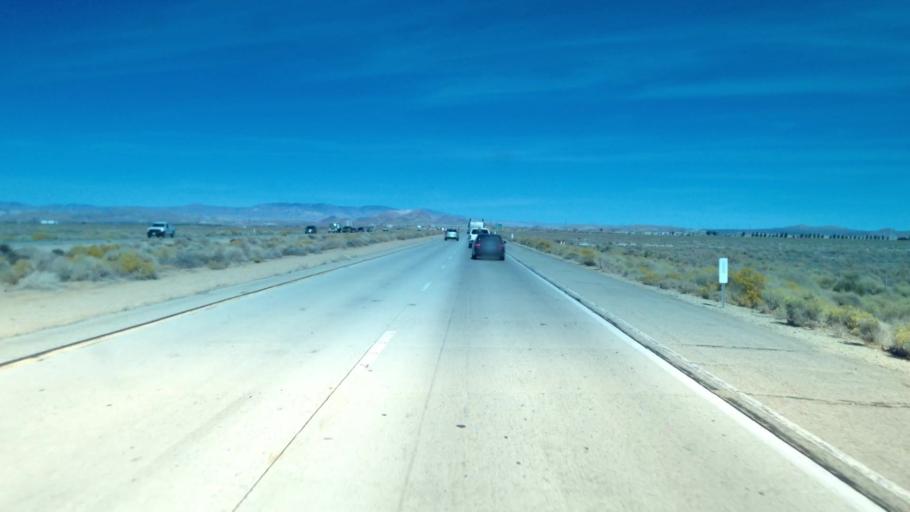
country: US
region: California
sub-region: Los Angeles County
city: Lancaster
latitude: 34.7643
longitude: -118.1704
